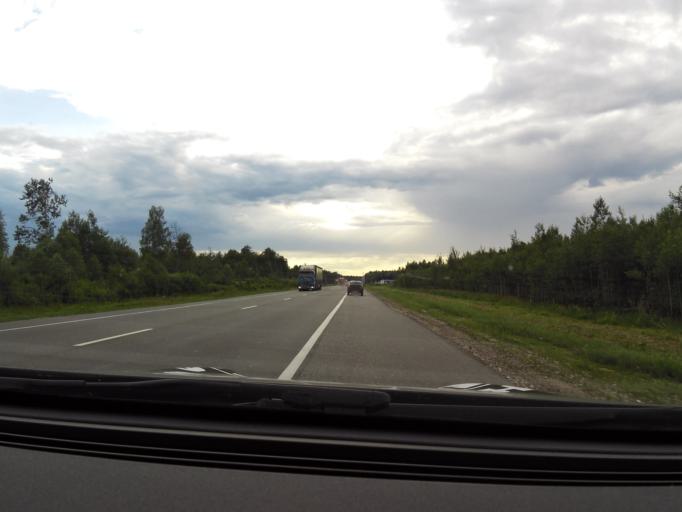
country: RU
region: Vladimir
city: Raduzhnyy
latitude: 56.0718
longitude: 40.2506
